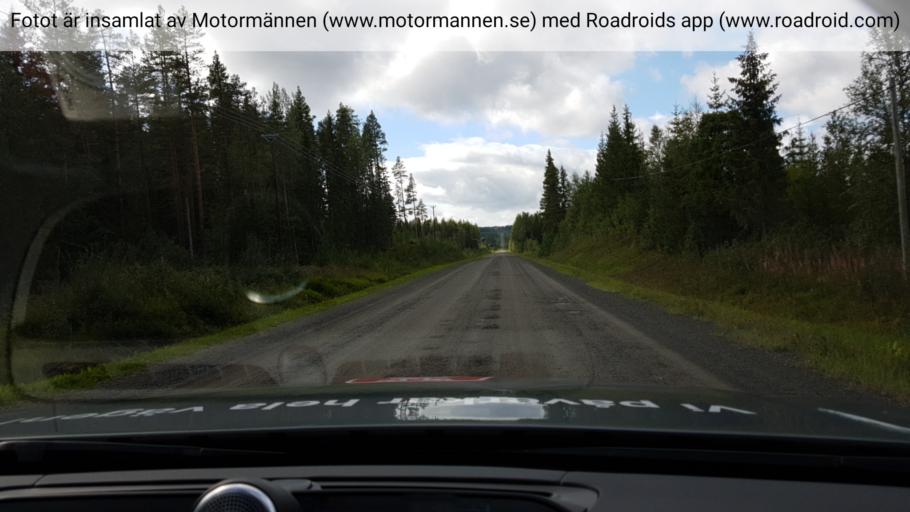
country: SE
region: Jaemtland
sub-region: Stroemsunds Kommun
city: Stroemsund
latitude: 63.6231
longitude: 15.1610
